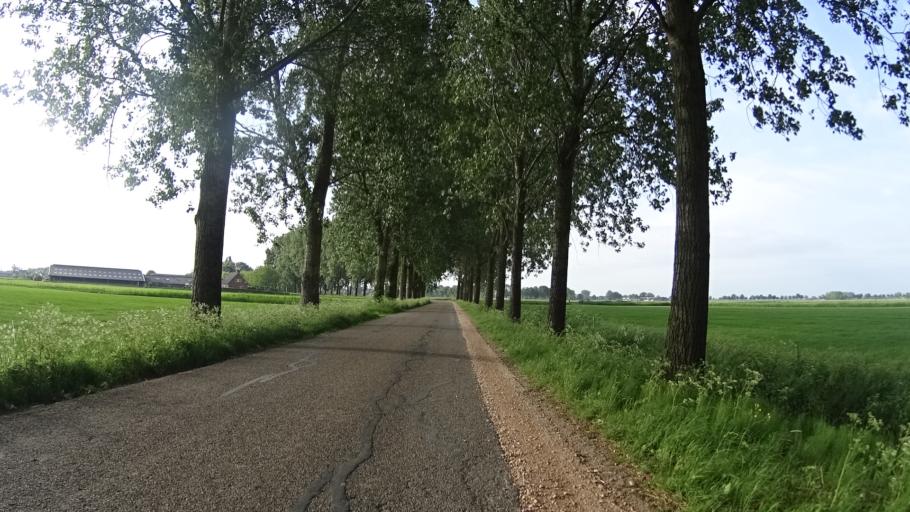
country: NL
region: North Brabant
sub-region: Gemeente Heusden
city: Heusden
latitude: 51.7204
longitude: 5.1608
